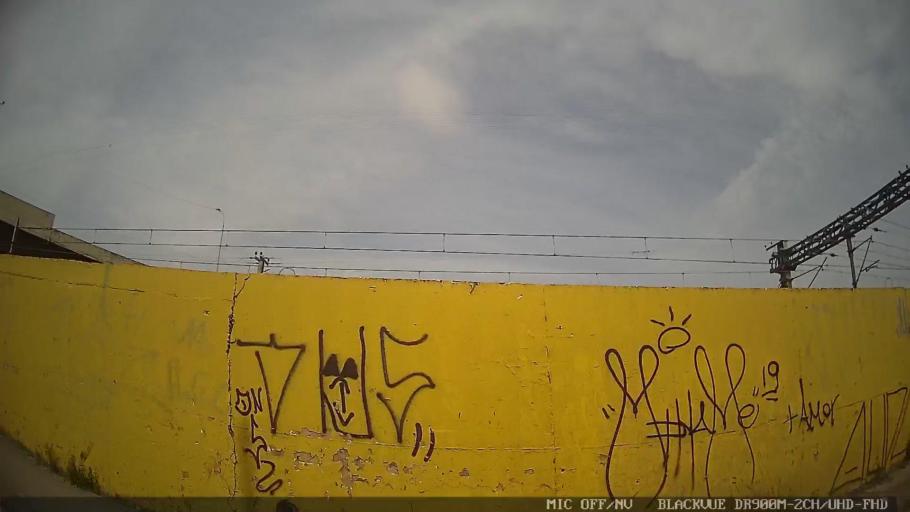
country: BR
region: Sao Paulo
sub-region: Poa
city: Poa
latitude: -23.5116
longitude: -46.3379
